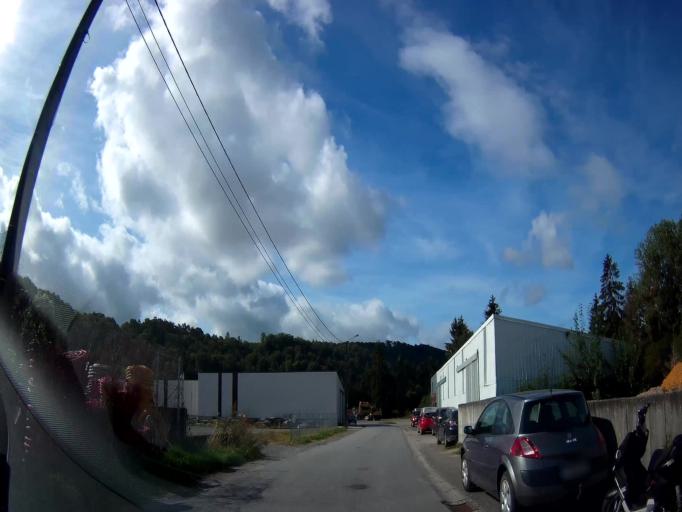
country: BE
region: Wallonia
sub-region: Province de Namur
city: Rochefort
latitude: 50.1575
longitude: 5.2173
